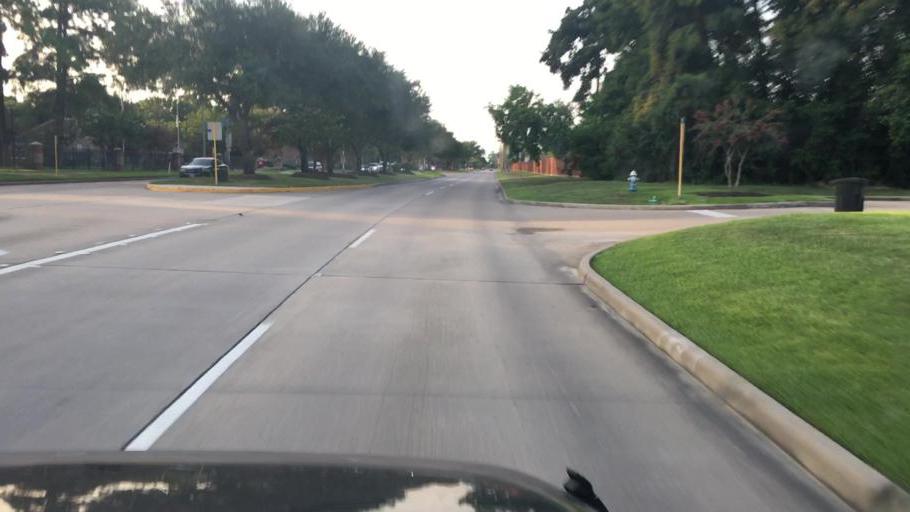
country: US
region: Texas
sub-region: Harris County
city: Atascocita
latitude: 29.9745
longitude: -95.2121
